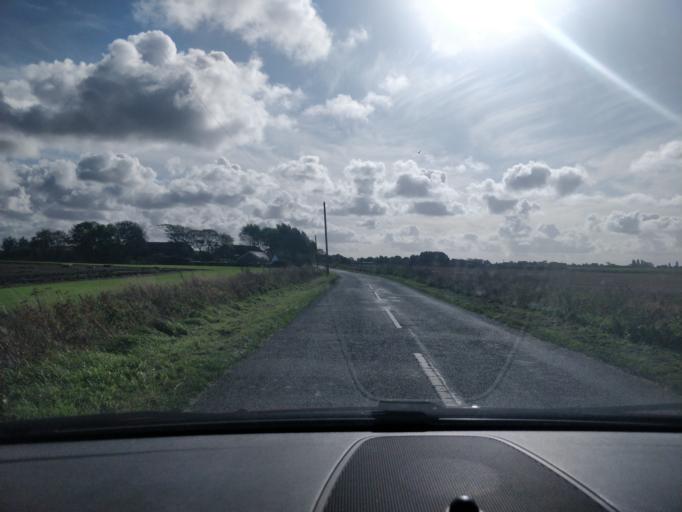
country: GB
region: England
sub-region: Lancashire
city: Banks
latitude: 53.6280
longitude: -2.9413
